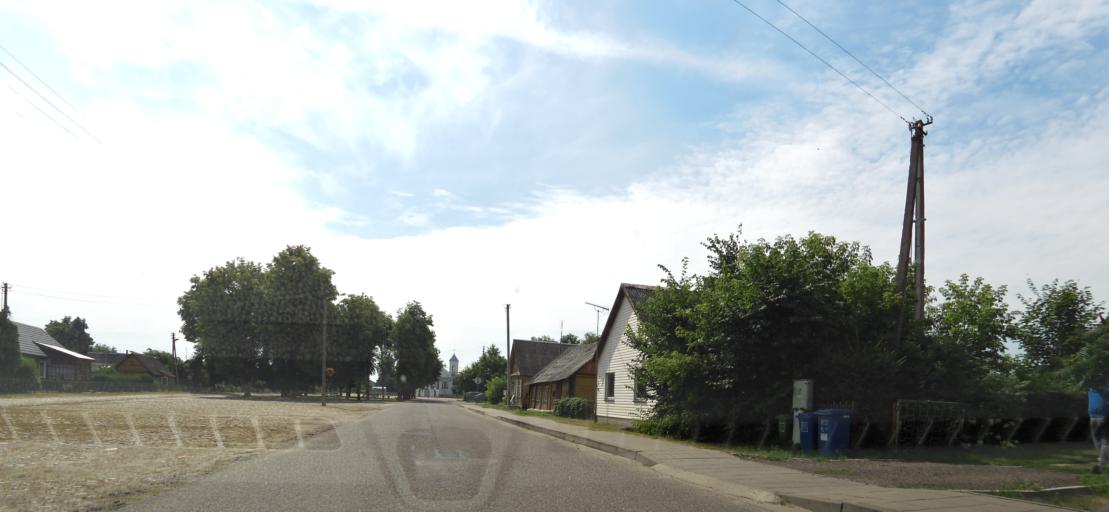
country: LT
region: Vilnius County
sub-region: Trakai
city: Rudiskes
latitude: 54.3605
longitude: 24.8402
